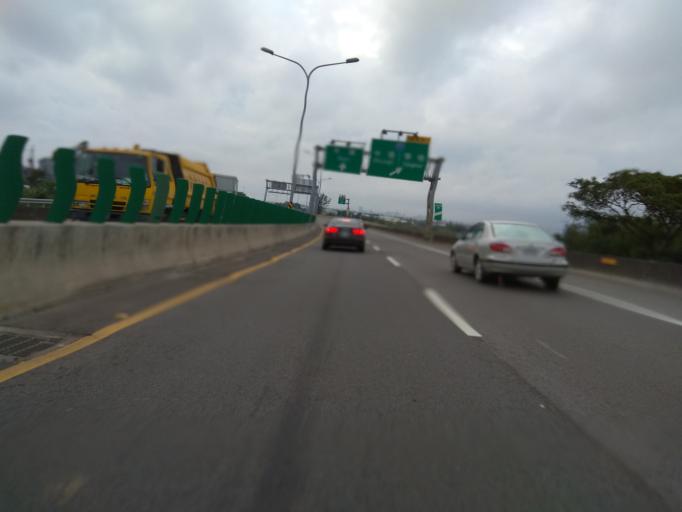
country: TW
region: Taiwan
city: Taoyuan City
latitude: 24.9605
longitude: 121.1369
